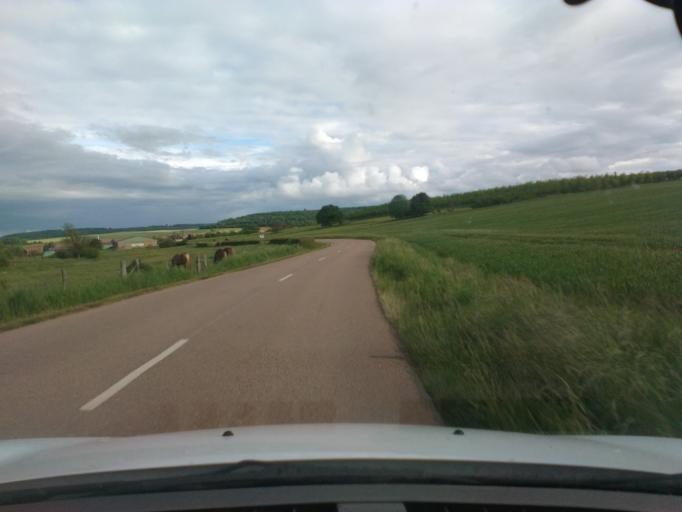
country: FR
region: Lorraine
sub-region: Departement des Vosges
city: Mirecourt
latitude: 48.3216
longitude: 6.0454
